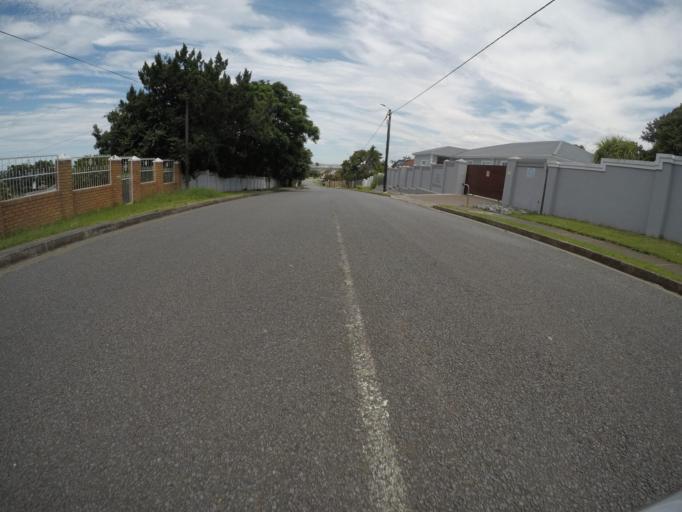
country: ZA
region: Eastern Cape
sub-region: Buffalo City Metropolitan Municipality
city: East London
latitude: -33.0399
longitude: 27.8533
